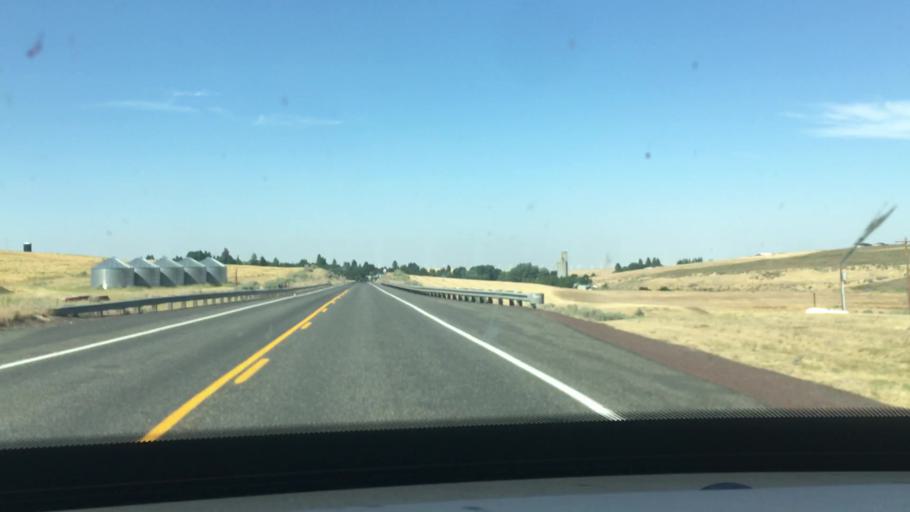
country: US
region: Oregon
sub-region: Sherman County
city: Moro
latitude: 45.4742
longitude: -120.7435
